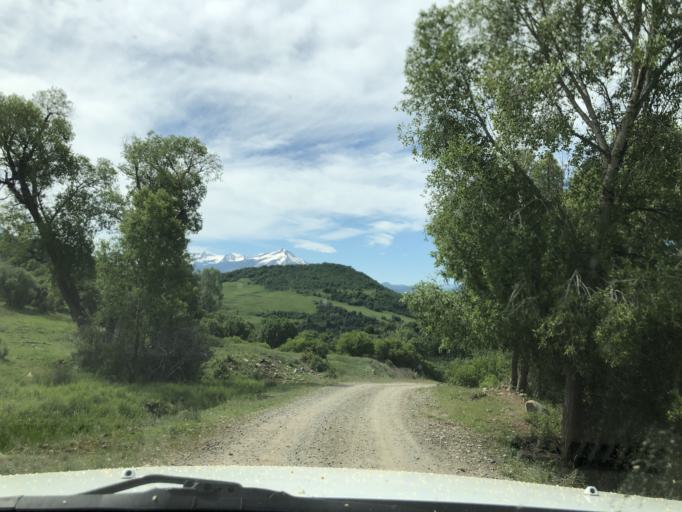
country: US
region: Colorado
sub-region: Delta County
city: Paonia
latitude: 38.9997
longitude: -107.3460
